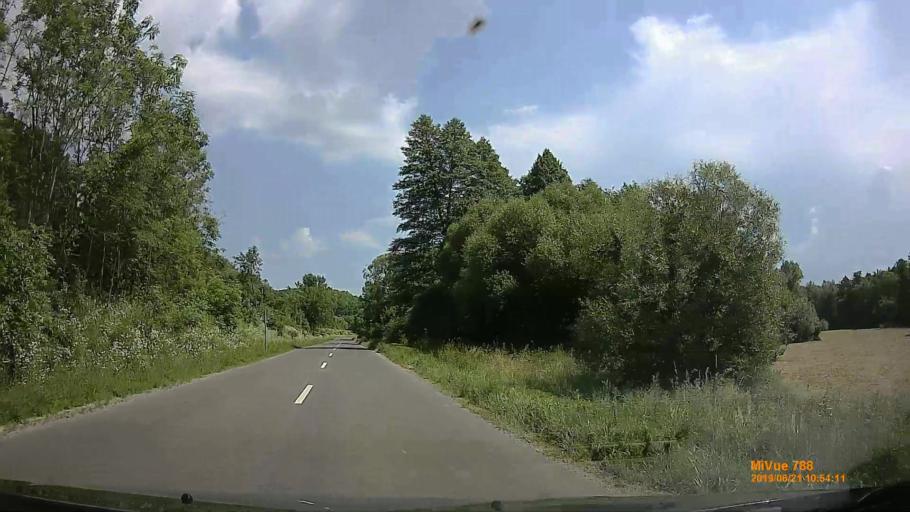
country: HU
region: Baranya
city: Buekkoesd
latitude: 46.1507
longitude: 18.0639
